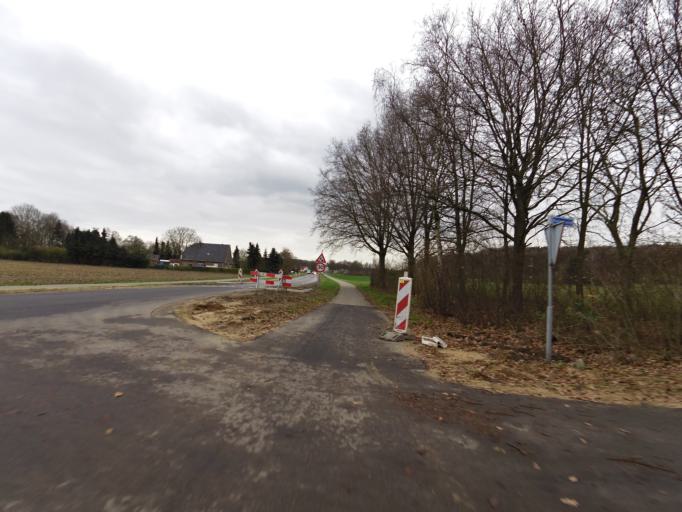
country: NL
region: Gelderland
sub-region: Gemeente Montferland
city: s-Heerenberg
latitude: 51.9132
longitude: 6.2589
